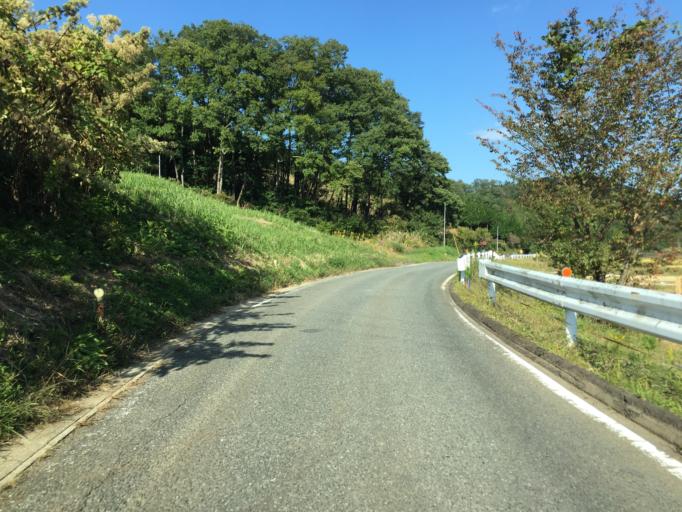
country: JP
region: Fukushima
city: Fukushima-shi
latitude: 37.6750
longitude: 140.4346
